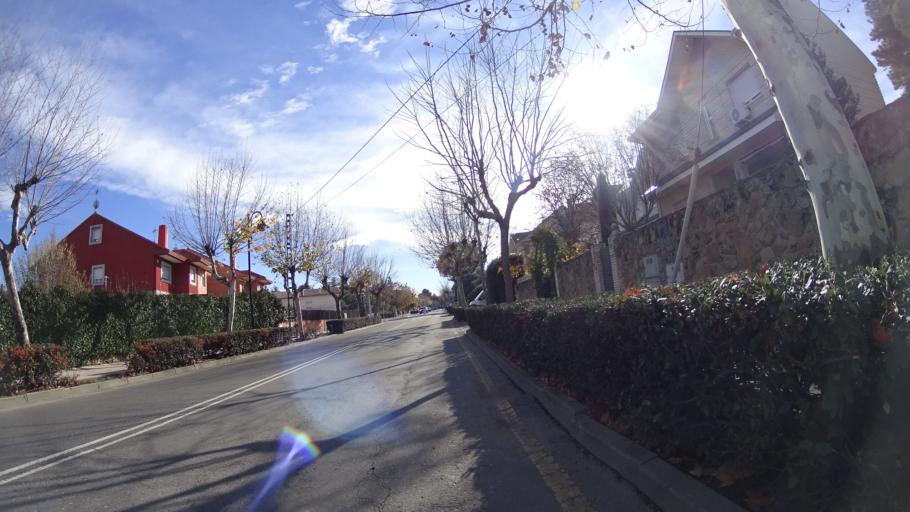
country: ES
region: Madrid
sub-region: Provincia de Madrid
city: Galapagar
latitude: 40.5773
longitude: -4.0103
